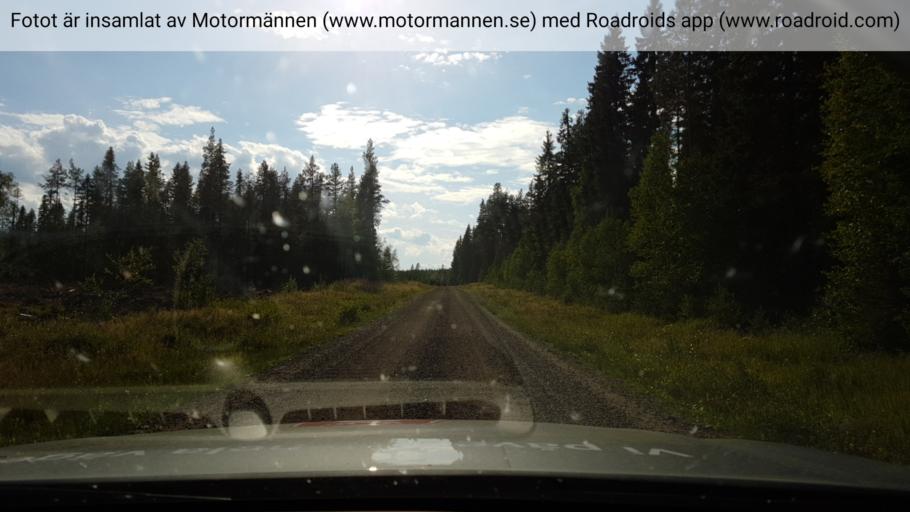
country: SE
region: Jaemtland
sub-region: Stroemsunds Kommun
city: Stroemsund
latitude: 63.7272
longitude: 16.1069
